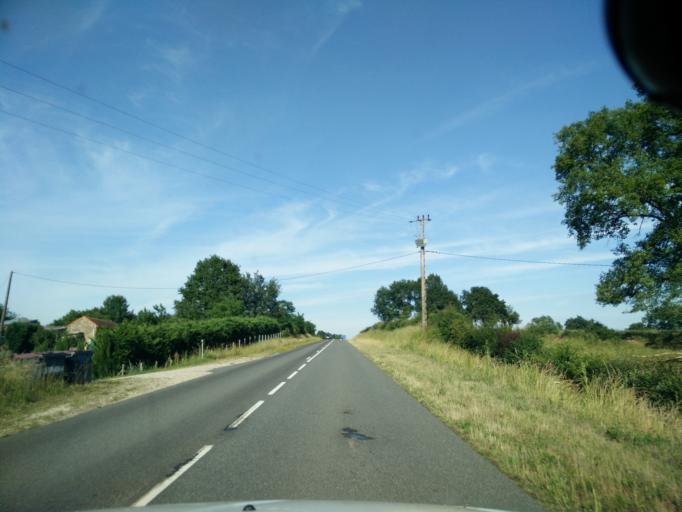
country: FR
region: Auvergne
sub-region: Departement de l'Allier
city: Souvigny
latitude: 46.5252
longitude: 3.1558
